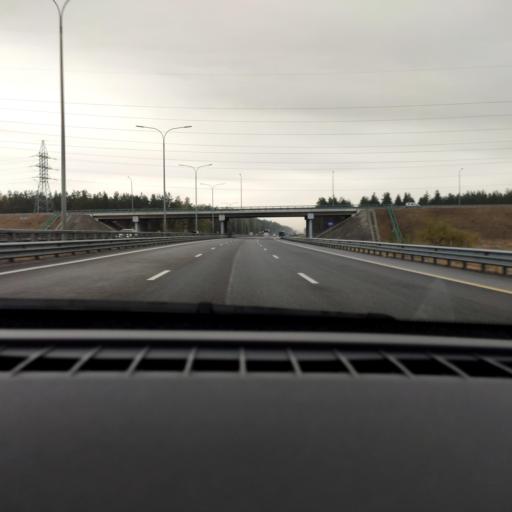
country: RU
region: Voronezj
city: Somovo
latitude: 51.7281
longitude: 39.3112
